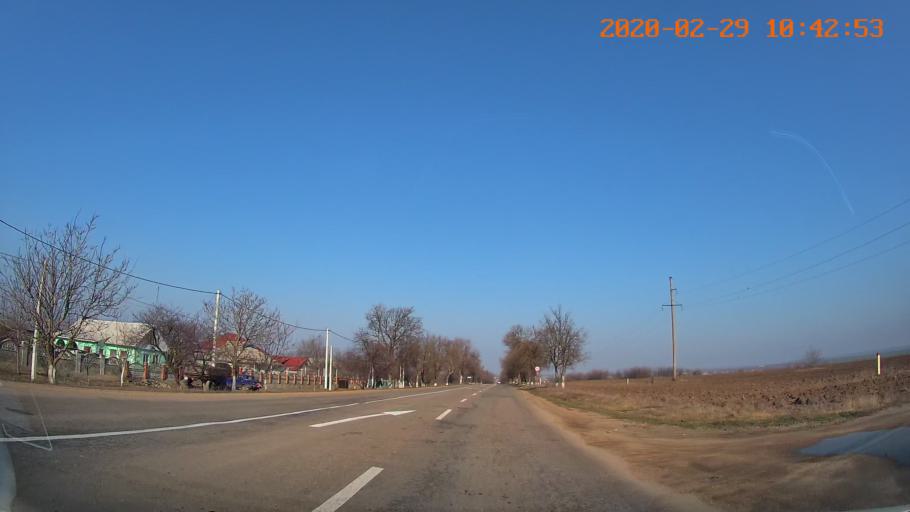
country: MD
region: Telenesti
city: Grigoriopol
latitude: 47.0552
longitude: 29.4061
